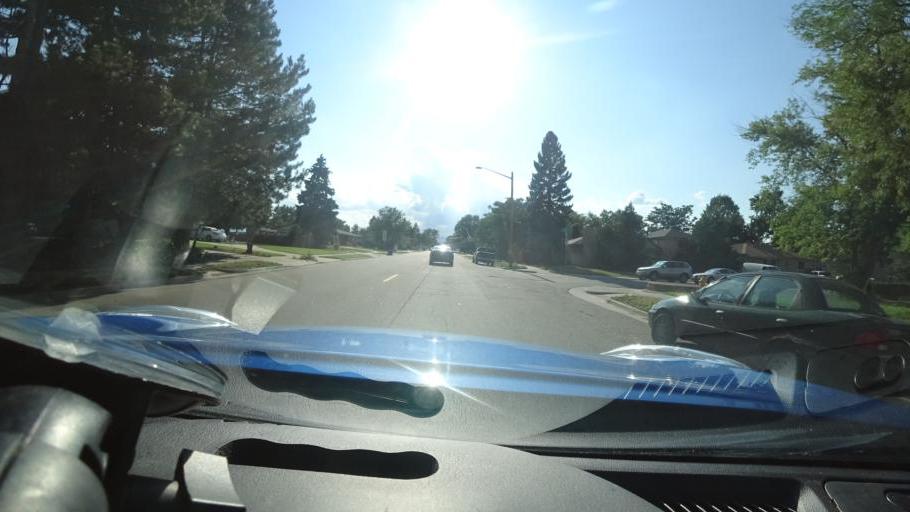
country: US
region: Colorado
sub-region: Arapahoe County
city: Sheridan
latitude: 39.6792
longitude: -105.0477
